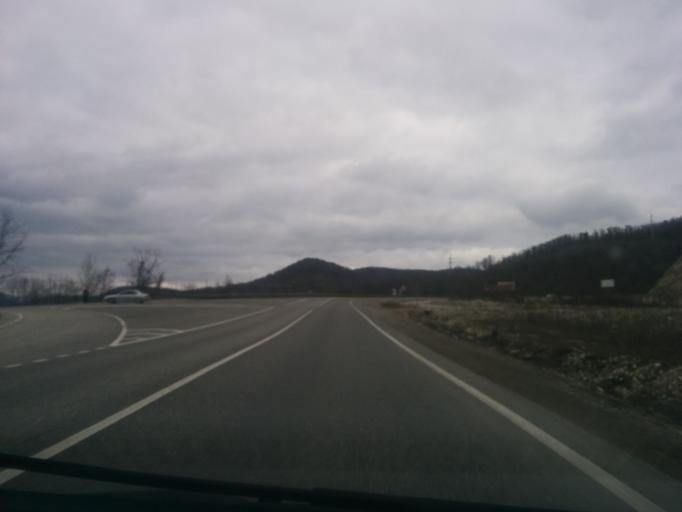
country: RU
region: Krasnodarskiy
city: Novomikhaylovskiy
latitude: 44.2574
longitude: 38.8781
